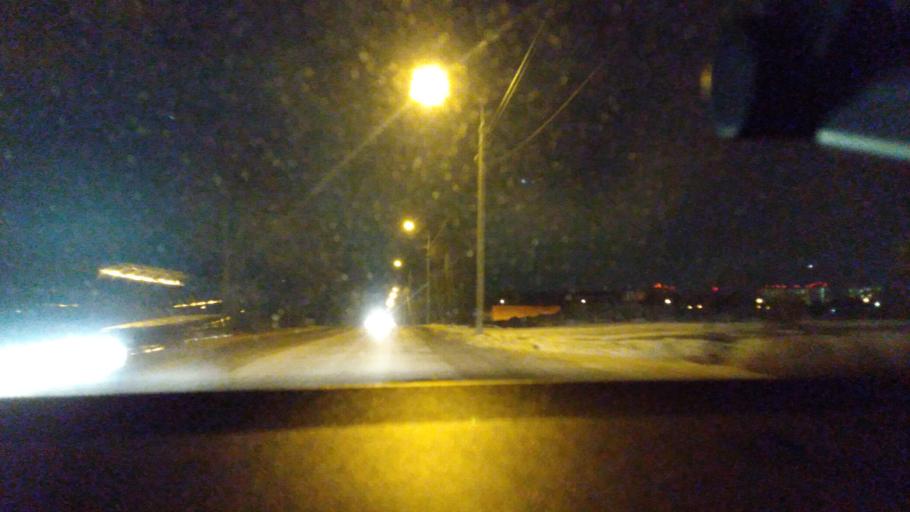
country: RU
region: Moskovskaya
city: Zheleznodorozhnyy
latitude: 55.7407
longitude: 38.0403
